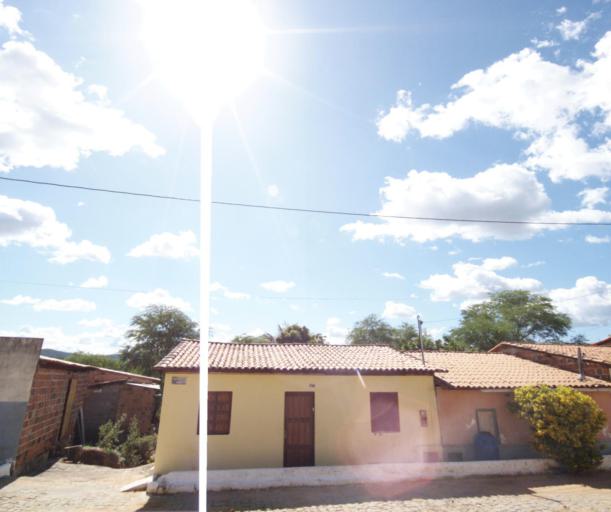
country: BR
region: Bahia
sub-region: Pocoes
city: Pocoes
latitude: -14.2413
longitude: -40.7737
